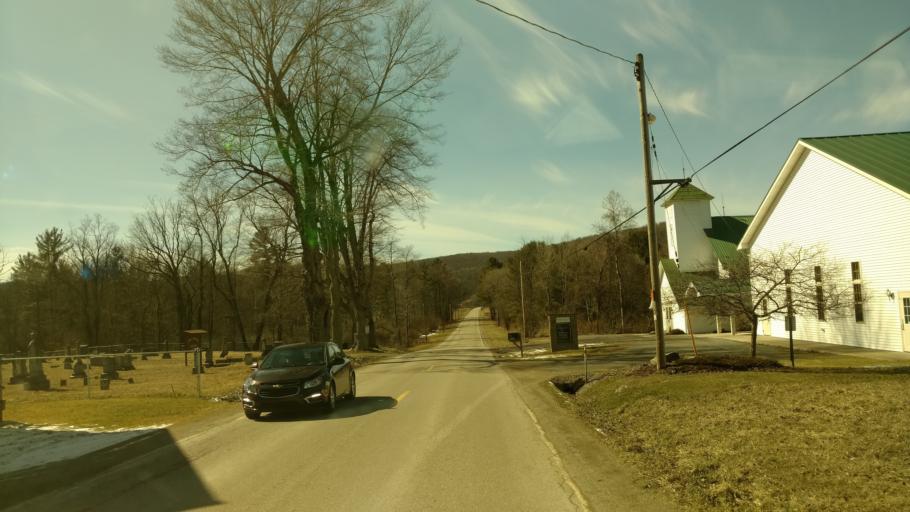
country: US
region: New York
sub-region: Allegany County
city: Wellsville
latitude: 42.0486
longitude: -77.9192
